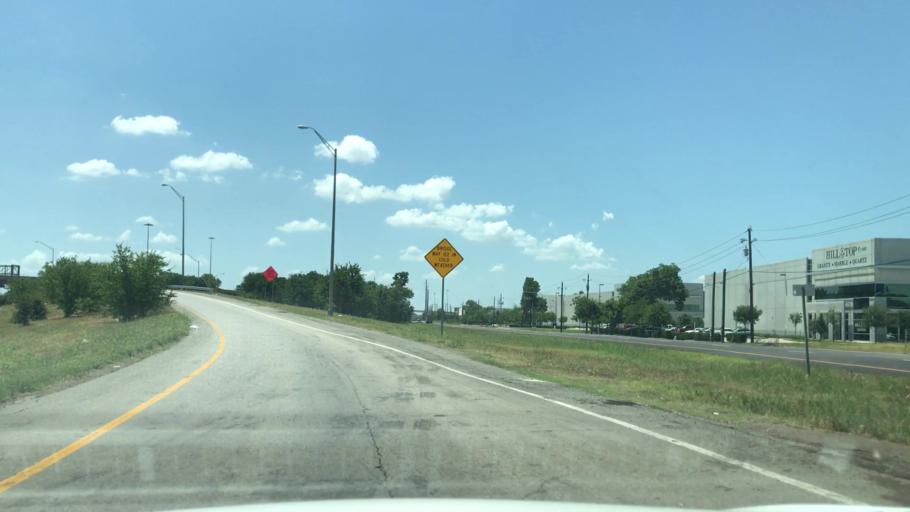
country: US
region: Texas
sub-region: Dallas County
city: Farmers Branch
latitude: 32.9200
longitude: -96.9002
